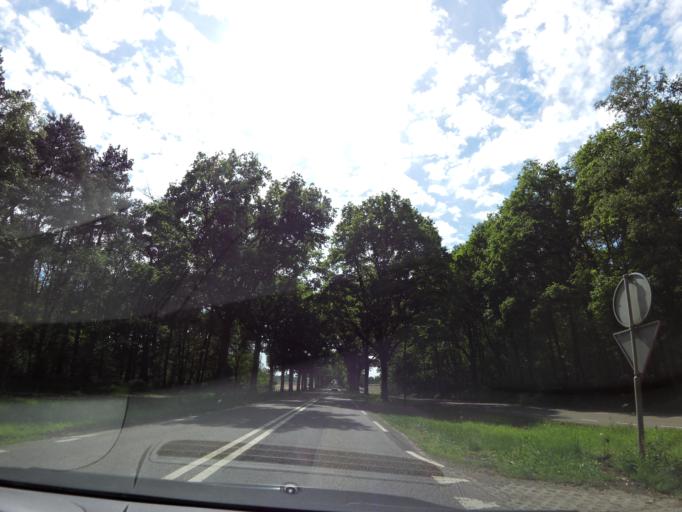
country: NL
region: Limburg
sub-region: Gemeente Leudal
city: Haelen
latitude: 51.2212
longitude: 5.9374
